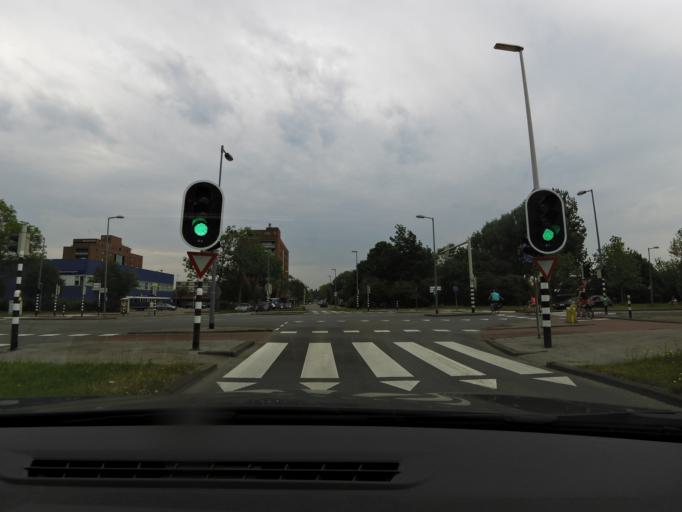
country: NL
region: South Holland
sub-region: Gemeente Spijkenisse
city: Spijkenisse
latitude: 51.8662
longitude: 4.3603
